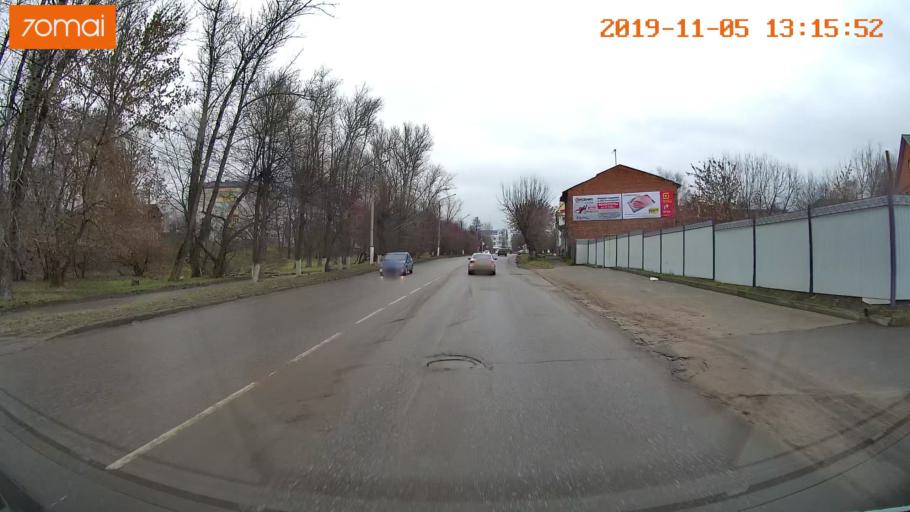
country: RU
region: Ivanovo
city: Shuya
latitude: 56.8513
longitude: 41.3700
